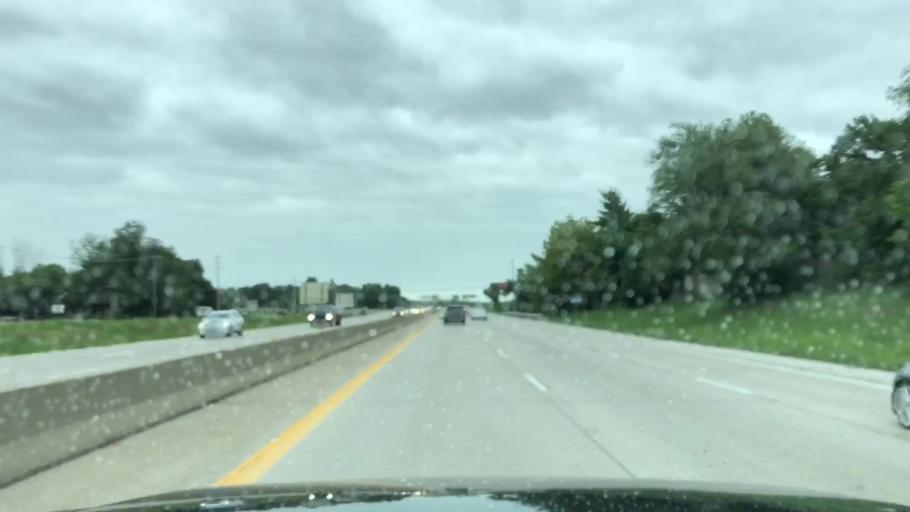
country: US
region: Missouri
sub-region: Saint Louis County
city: Manchester
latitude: 38.6310
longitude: -90.5141
